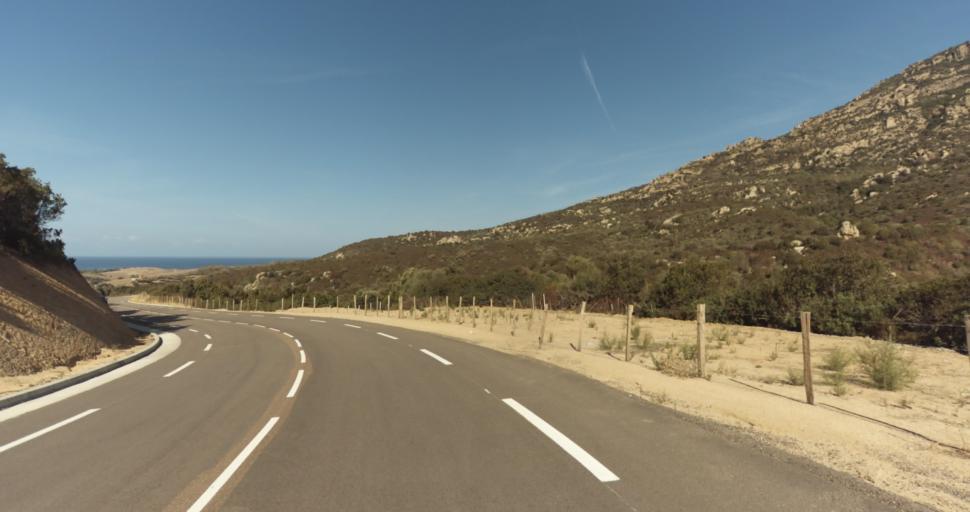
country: FR
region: Corsica
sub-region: Departement de la Corse-du-Sud
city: Ajaccio
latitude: 41.9312
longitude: 8.6633
